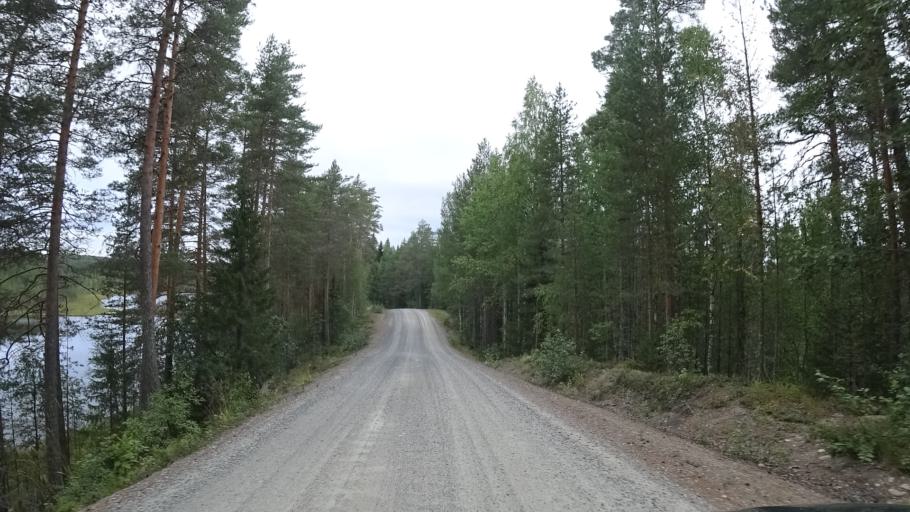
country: FI
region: North Karelia
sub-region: Pielisen Karjala
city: Lieksa
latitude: 63.2314
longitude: 30.3726
